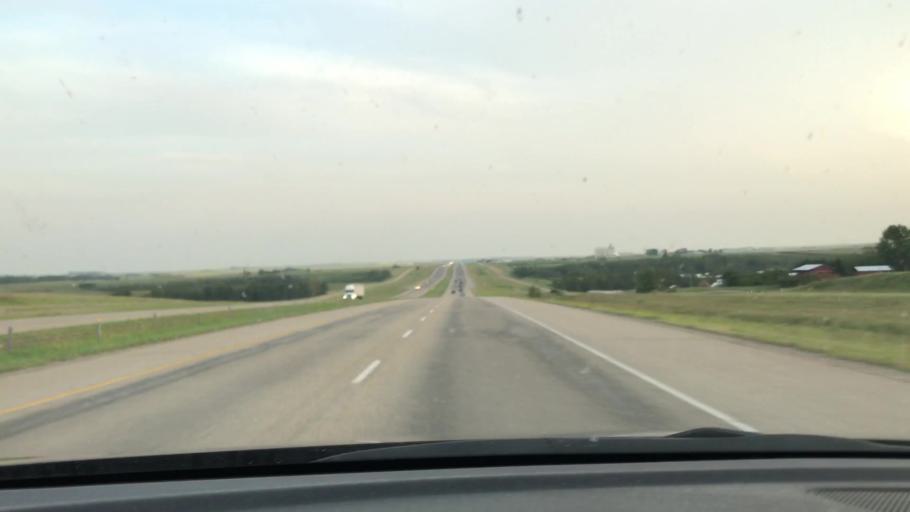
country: CA
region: Alberta
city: Carstairs
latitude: 51.5233
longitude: -114.0254
